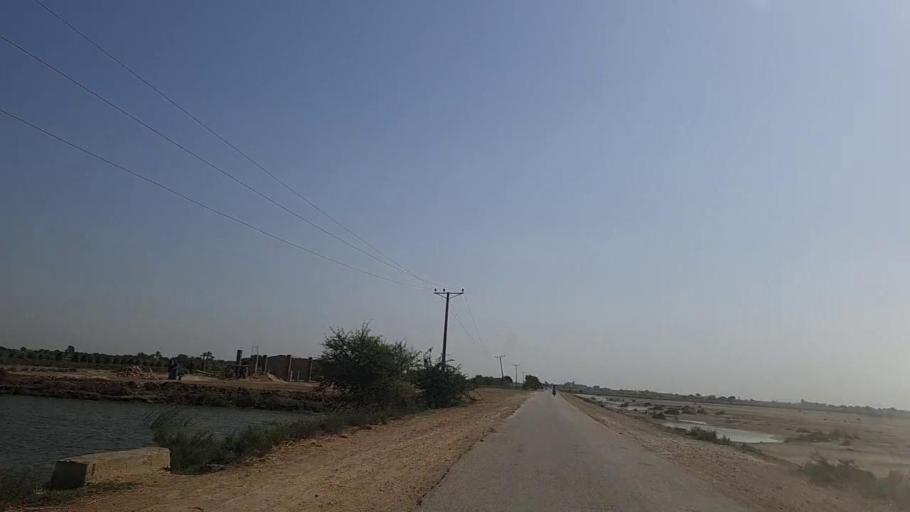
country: PK
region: Sindh
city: Mirpur Batoro
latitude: 24.6298
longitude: 68.2934
